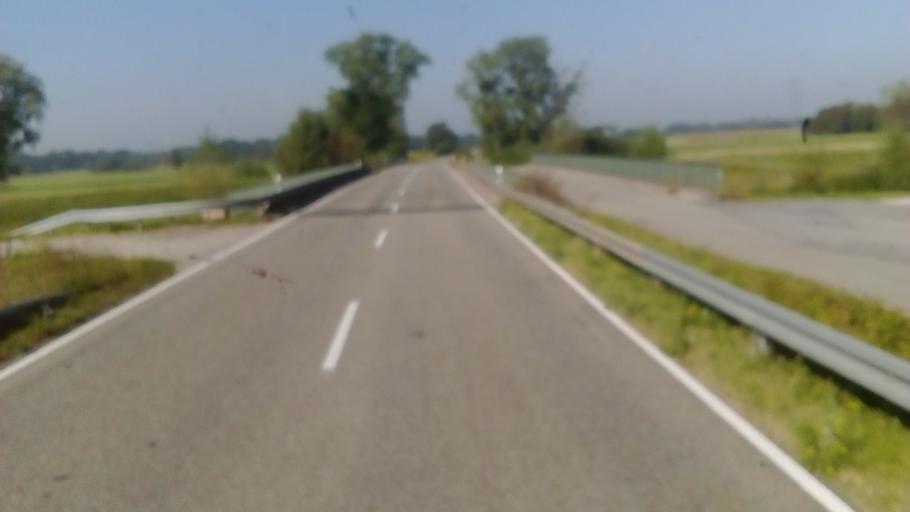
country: DE
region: Baden-Wuerttemberg
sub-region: Freiburg Region
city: Rheinau
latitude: 48.6505
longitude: 7.9773
